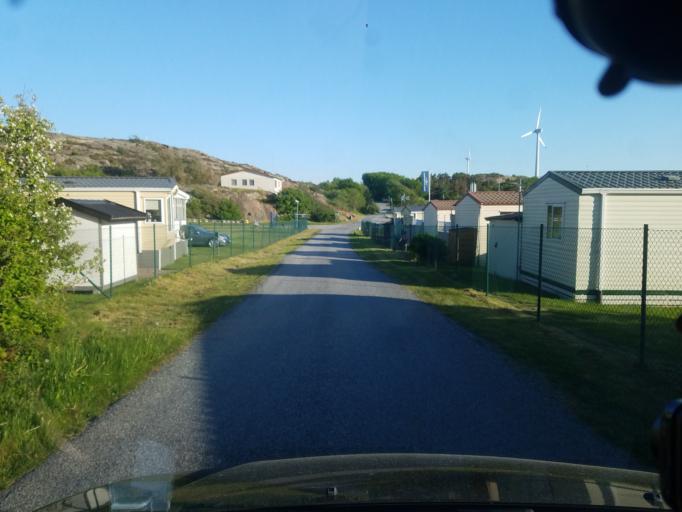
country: SE
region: Vaestra Goetaland
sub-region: Lysekils Kommun
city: Lysekil
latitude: 58.2983
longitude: 11.4482
